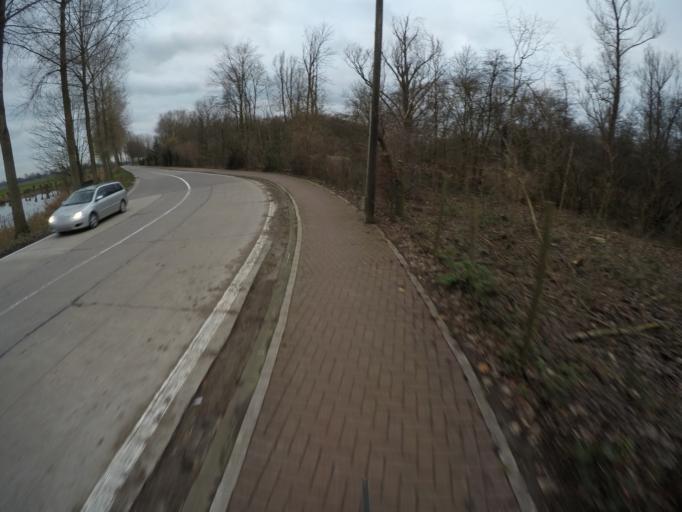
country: BE
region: Flanders
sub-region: Provincie Oost-Vlaanderen
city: Sint-Gillis-Waas
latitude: 51.2434
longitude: 4.1466
